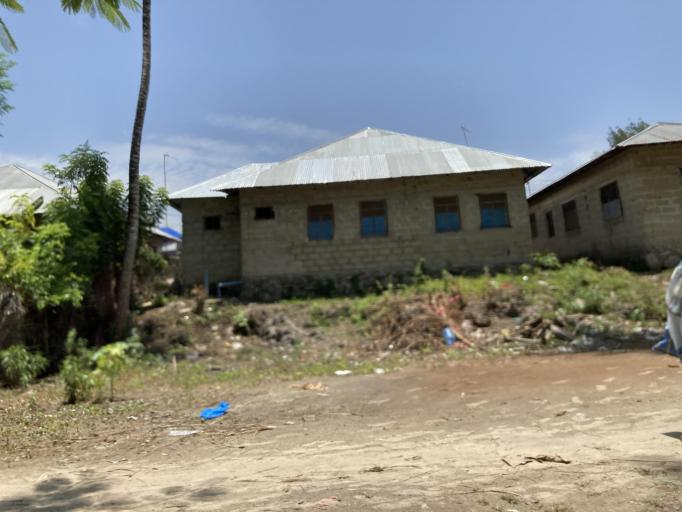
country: TZ
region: Zanzibar North
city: Gamba
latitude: -5.9259
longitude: 39.3578
